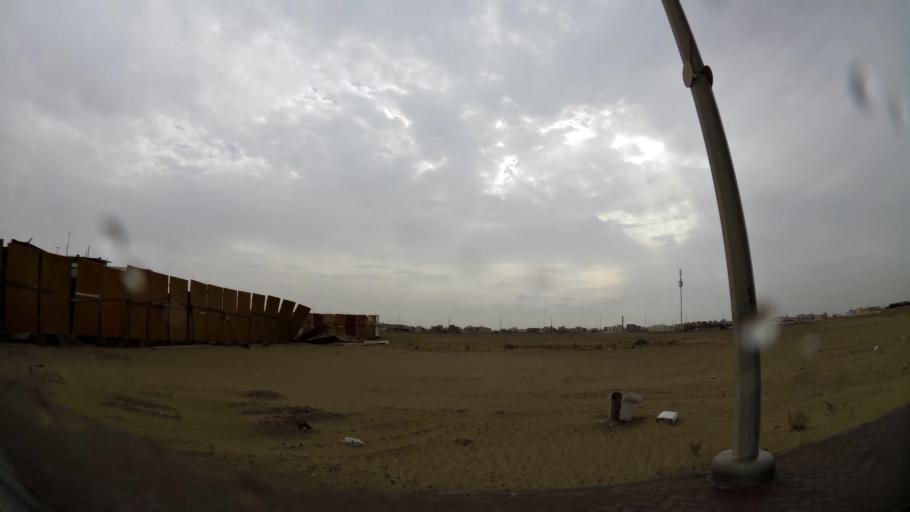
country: AE
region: Abu Dhabi
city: Abu Dhabi
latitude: 24.3668
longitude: 54.6352
